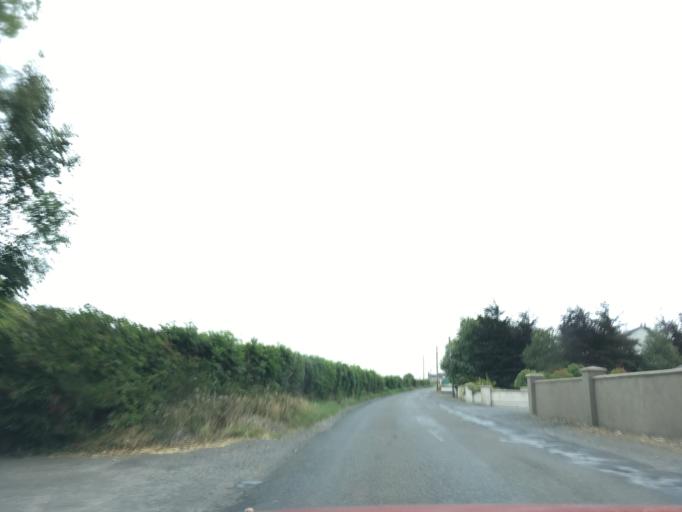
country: IE
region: Munster
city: Cashel
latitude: 52.4687
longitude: -7.8394
